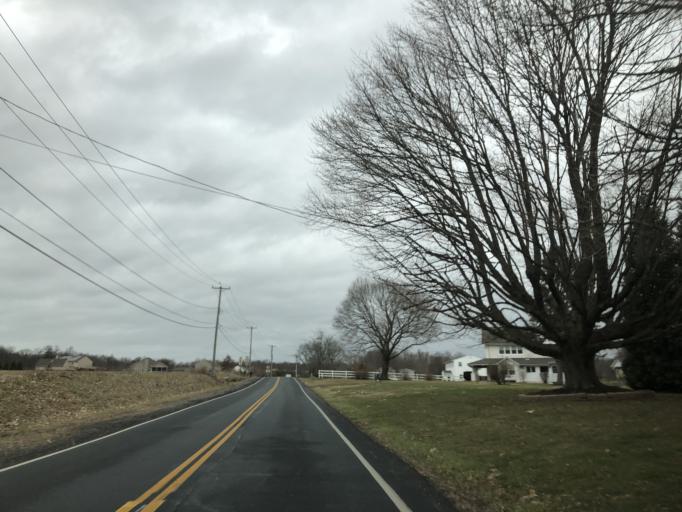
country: US
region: Pennsylvania
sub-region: Chester County
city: Oxford
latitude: 39.7011
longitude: -75.9321
